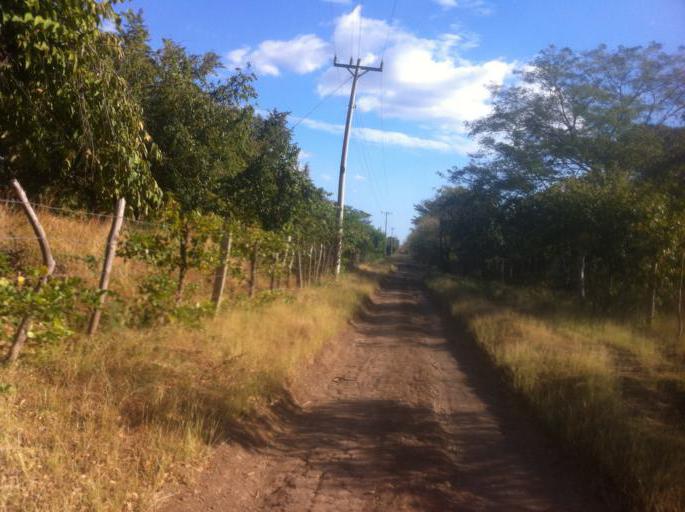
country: NI
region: Managua
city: Carlos Fonseca Amador
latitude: 11.9154
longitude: -86.5960
